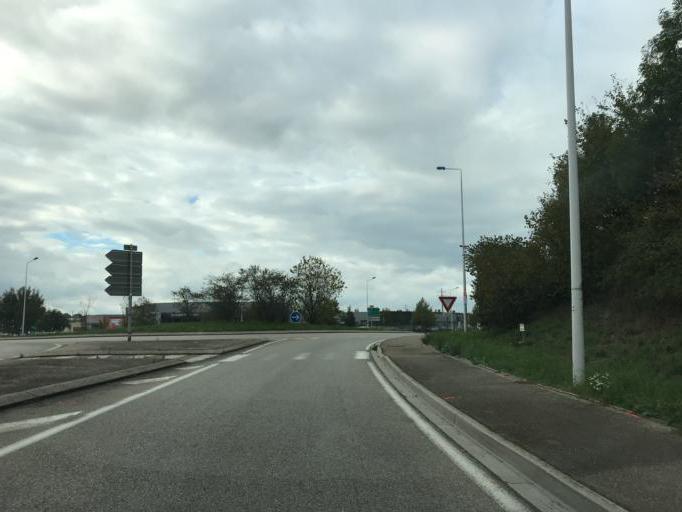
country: FR
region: Rhone-Alpes
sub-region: Departement de l'Ain
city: Bourg-en-Bresse
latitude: 46.2242
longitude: 5.2338
